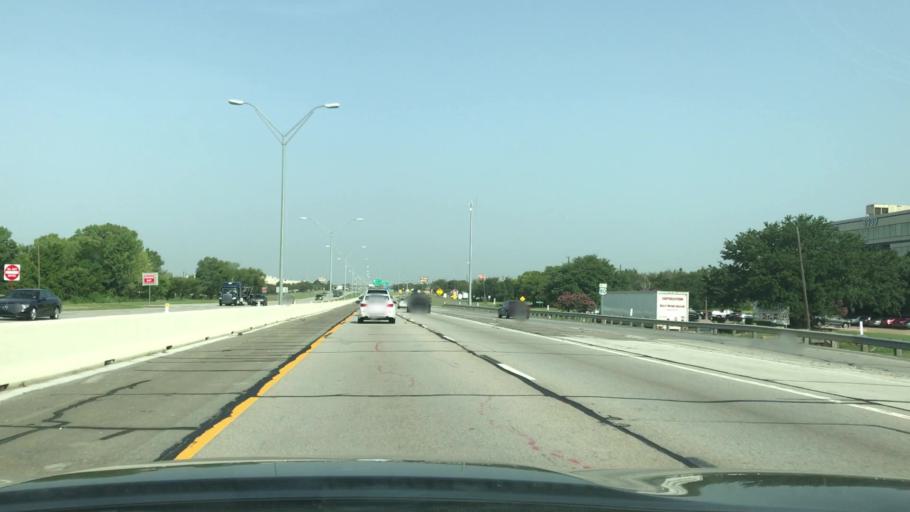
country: US
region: Texas
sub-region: Dallas County
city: Mesquite
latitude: 32.7940
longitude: -96.6577
